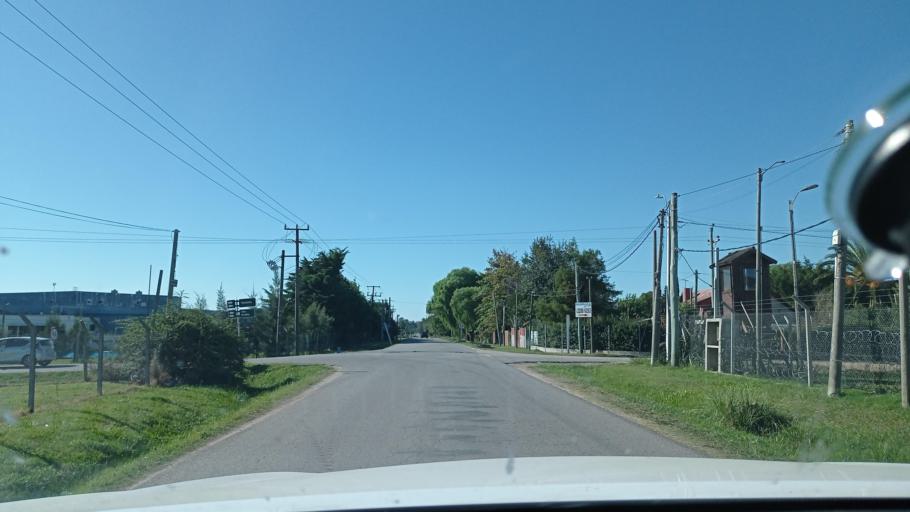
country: UY
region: Canelones
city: Pando
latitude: -34.7585
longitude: -55.9818
